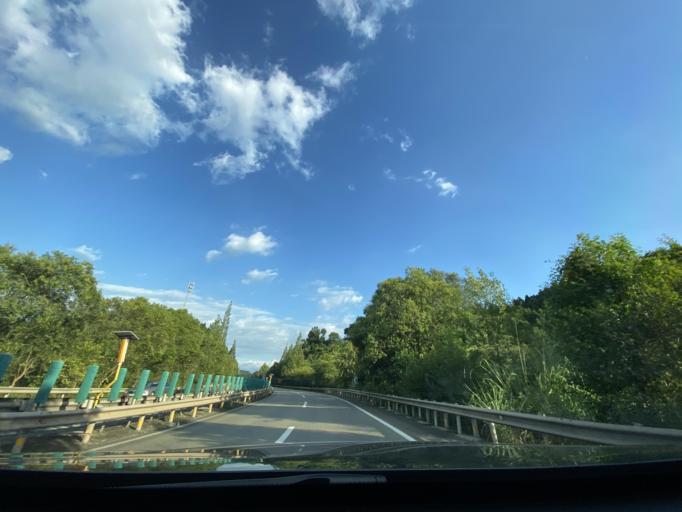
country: CN
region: Sichuan
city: Longquan
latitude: 30.5405
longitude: 104.3536
